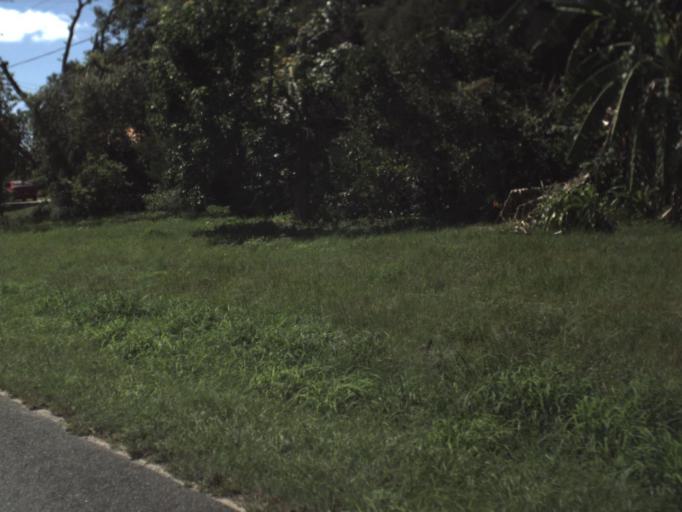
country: US
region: Florida
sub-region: Polk County
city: Dundee
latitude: 28.0180
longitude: -81.6085
